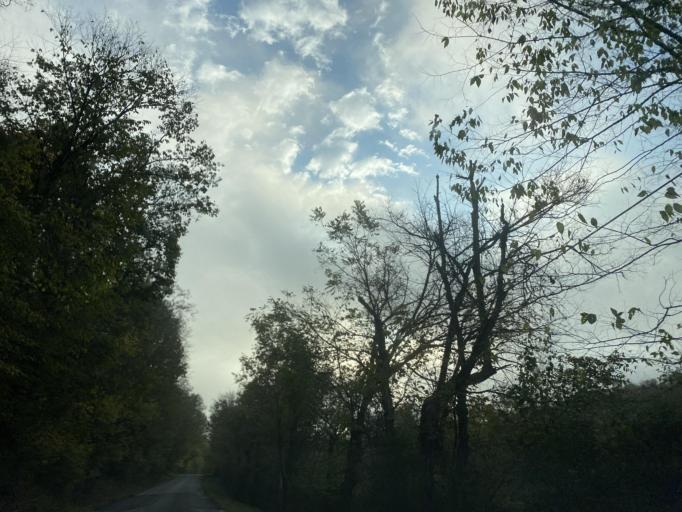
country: US
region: Kentucky
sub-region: Pendleton County
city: Falmouth
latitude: 38.7253
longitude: -84.3148
